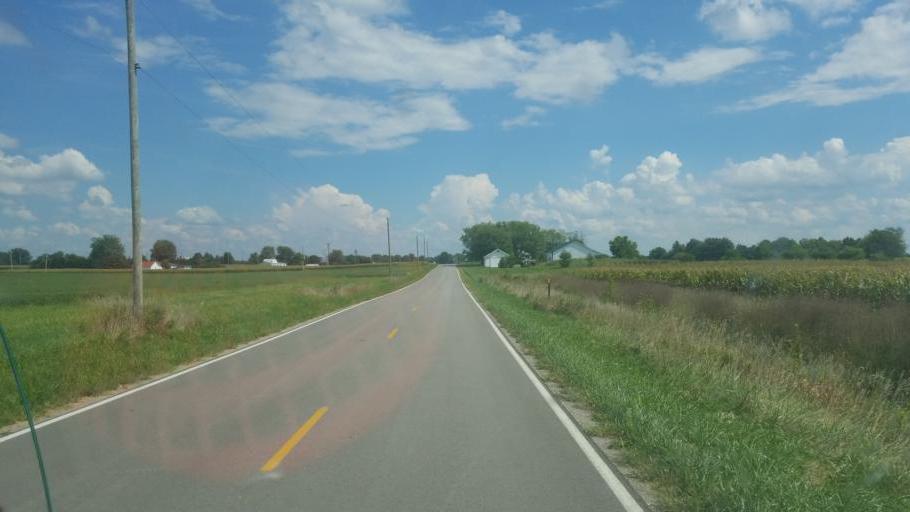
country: US
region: Ohio
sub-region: Hardin County
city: Forest
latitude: 40.8614
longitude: -83.4804
